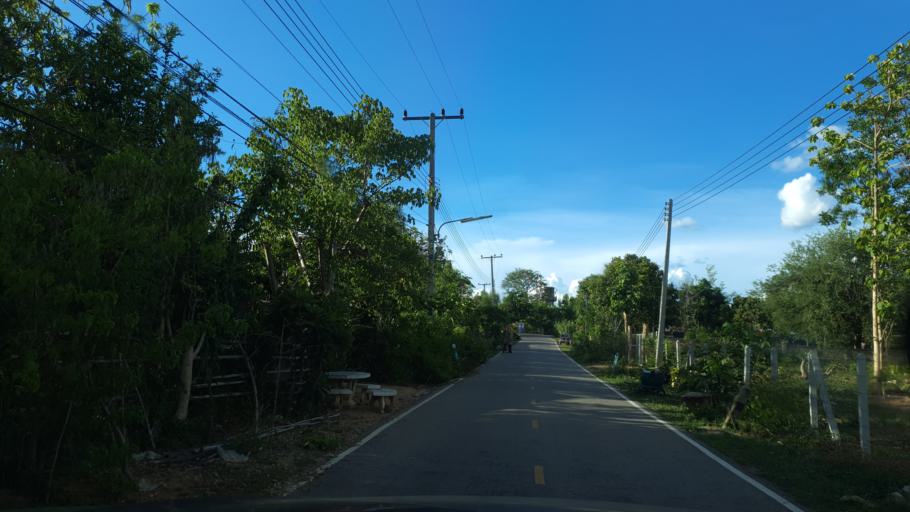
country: TH
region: Lampang
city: Sop Prap
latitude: 17.8739
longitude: 99.3092
